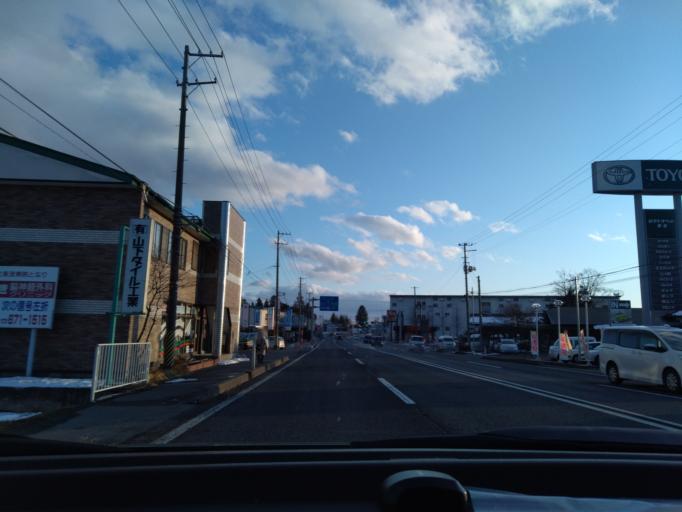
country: JP
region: Iwate
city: Morioka-shi
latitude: 39.5430
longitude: 141.1690
